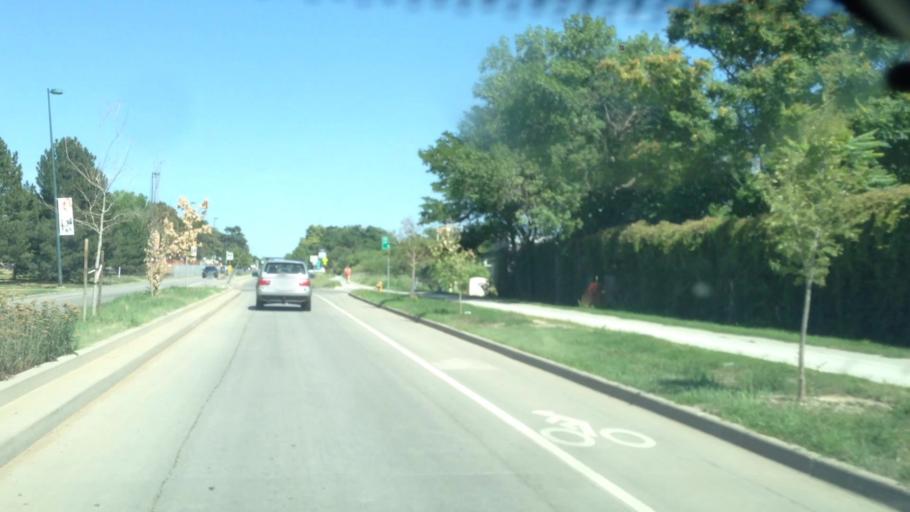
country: US
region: Colorado
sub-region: Denver County
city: Denver
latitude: 39.7512
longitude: -104.9516
